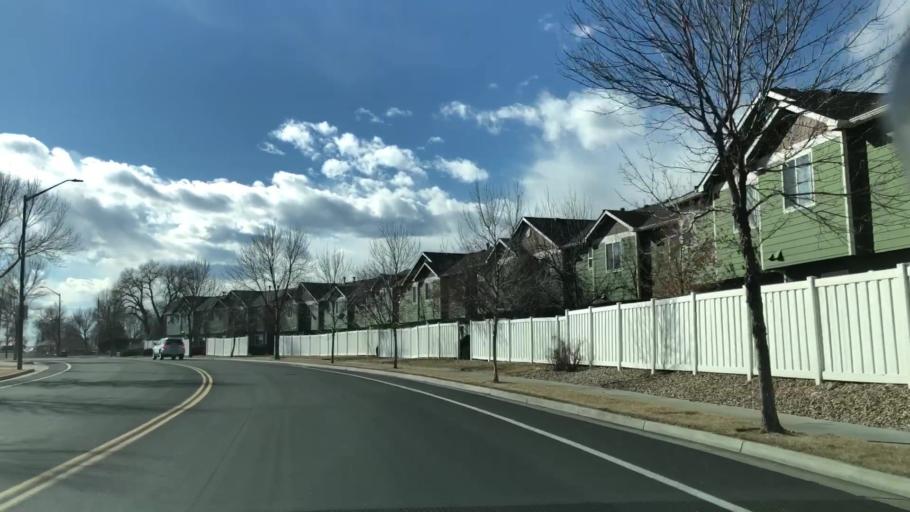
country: US
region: Colorado
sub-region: Larimer County
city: Fort Collins
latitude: 40.5973
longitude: -105.0050
